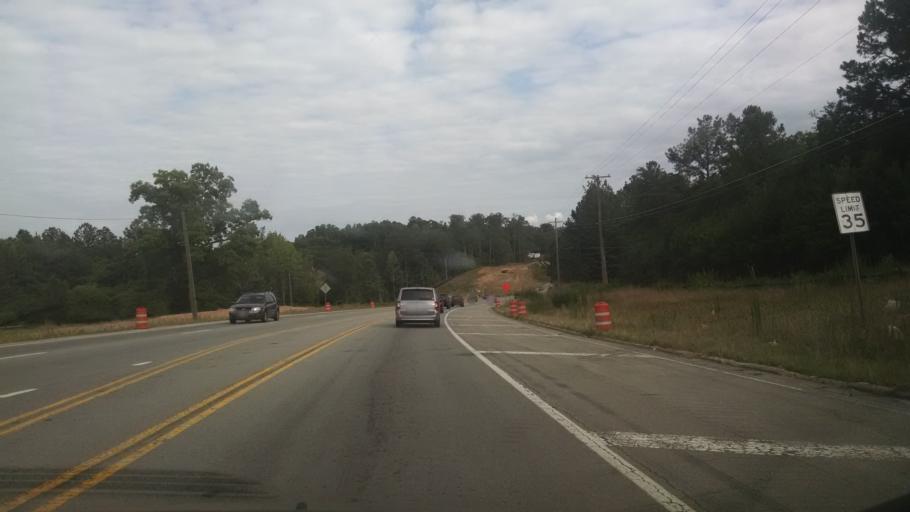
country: US
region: Georgia
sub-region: Gwinnett County
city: Sugar Hill
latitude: 34.1363
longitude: -84.1006
